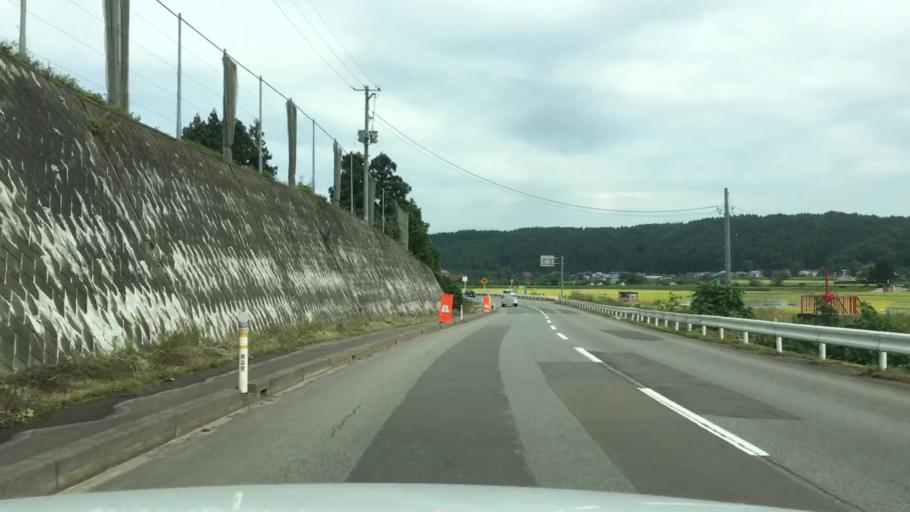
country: JP
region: Aomori
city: Shimokizukuri
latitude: 40.7522
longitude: 140.2296
